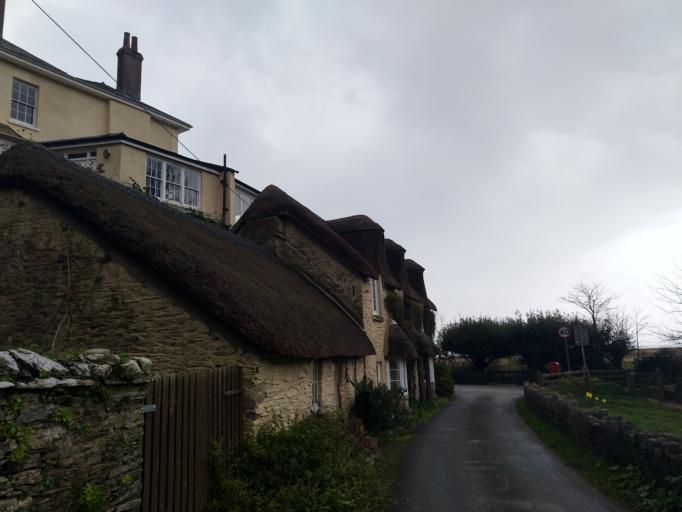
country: GB
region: England
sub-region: Devon
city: Dartmouth
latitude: 50.3202
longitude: -3.6125
